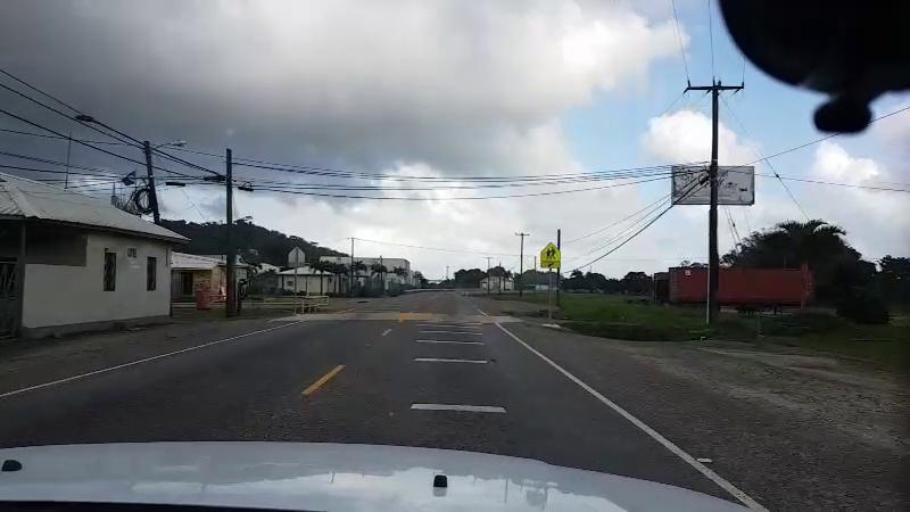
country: BZ
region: Stann Creek
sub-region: Dangriga
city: Dangriga
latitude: 16.9939
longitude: -88.3728
